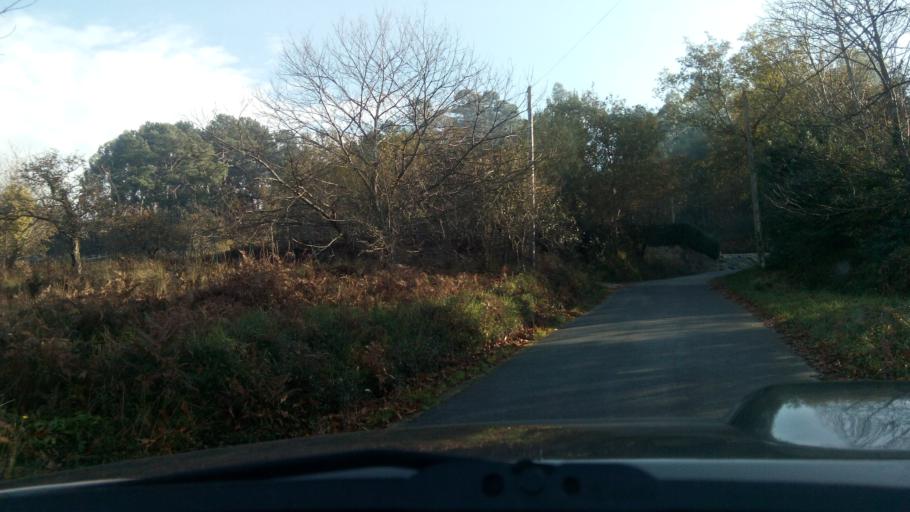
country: ES
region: Galicia
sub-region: Provincia de Pontevedra
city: Marin
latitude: 42.3567
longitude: -8.7292
